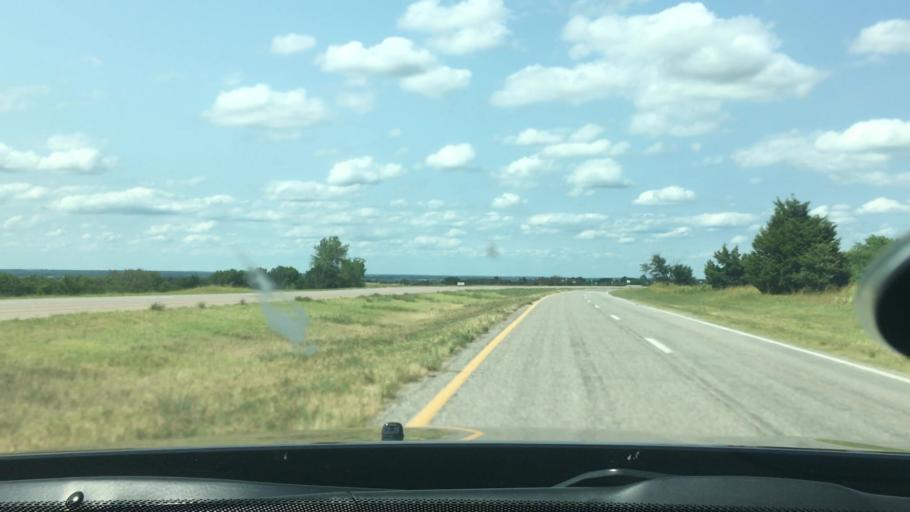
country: US
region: Oklahoma
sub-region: Pontotoc County
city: Ada
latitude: 34.7062
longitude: -96.7310
